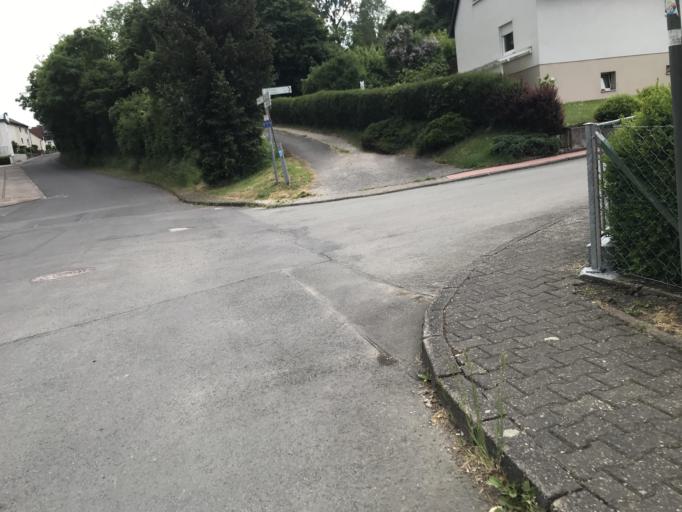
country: DE
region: Hesse
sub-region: Regierungsbezirk Kassel
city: Martinhagen
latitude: 51.2874
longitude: 9.3426
